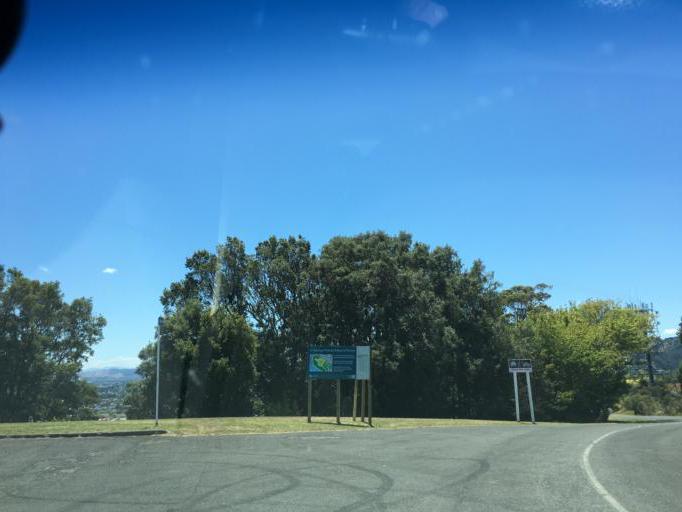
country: NZ
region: Gisborne
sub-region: Gisborne District
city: Gisborne
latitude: -38.6793
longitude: 178.0311
